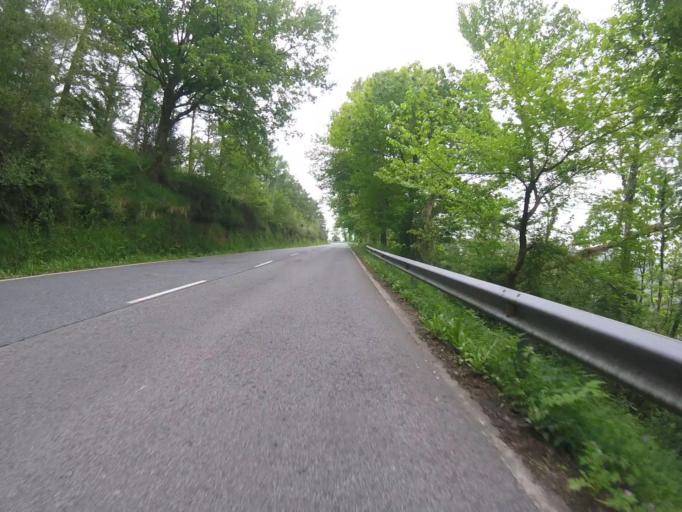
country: ES
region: Navarre
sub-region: Provincia de Navarra
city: Zugarramurdi
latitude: 43.2614
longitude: -1.4886
